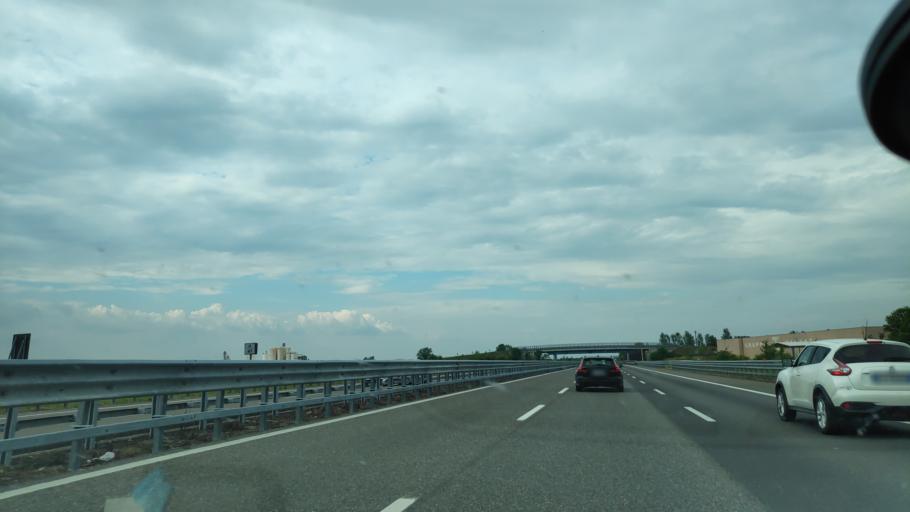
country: IT
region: Lombardy
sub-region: Provincia di Pavia
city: Silvano Pietra
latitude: 45.0366
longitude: 8.9396
